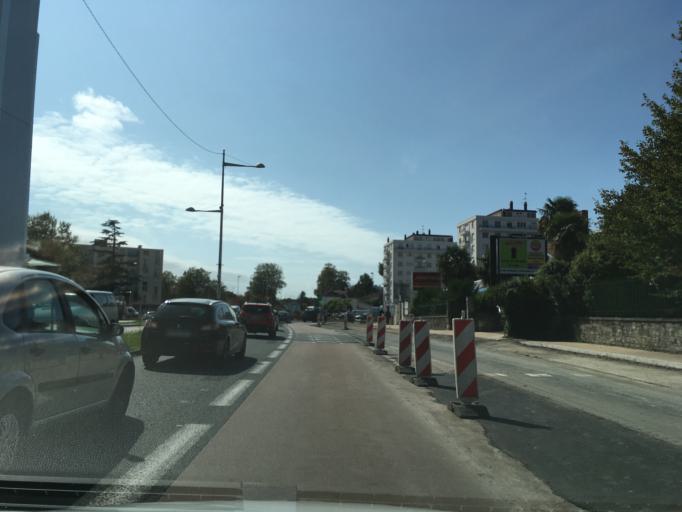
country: FR
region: Aquitaine
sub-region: Departement des Pyrenees-Atlantiques
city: Anglet
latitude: 43.4820
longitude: -1.5085
